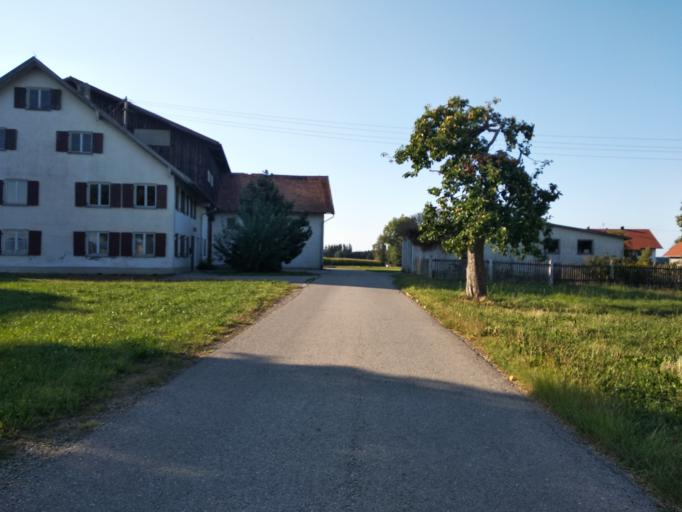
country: DE
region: Bavaria
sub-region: Swabia
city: Legau
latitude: 47.8648
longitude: 10.1161
